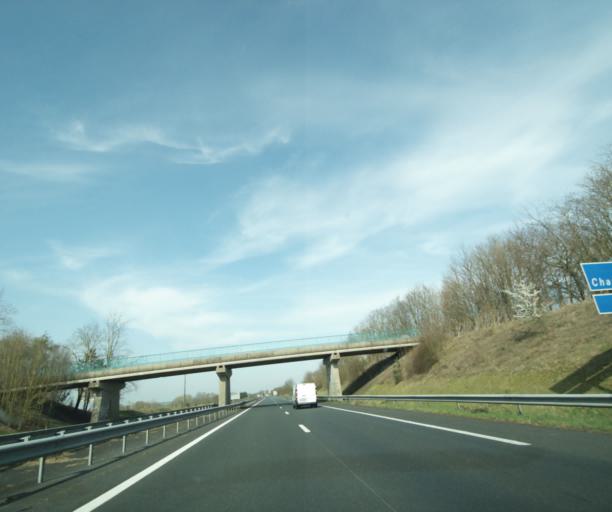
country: FR
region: Centre
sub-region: Departement de l'Indre
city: Vatan
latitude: 47.0375
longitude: 1.7936
